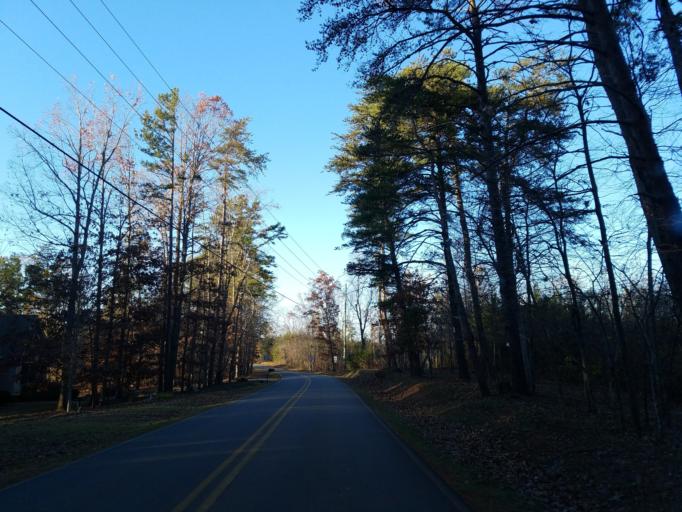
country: US
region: Georgia
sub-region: Pickens County
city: Nelson
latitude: 34.3897
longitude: -84.3703
